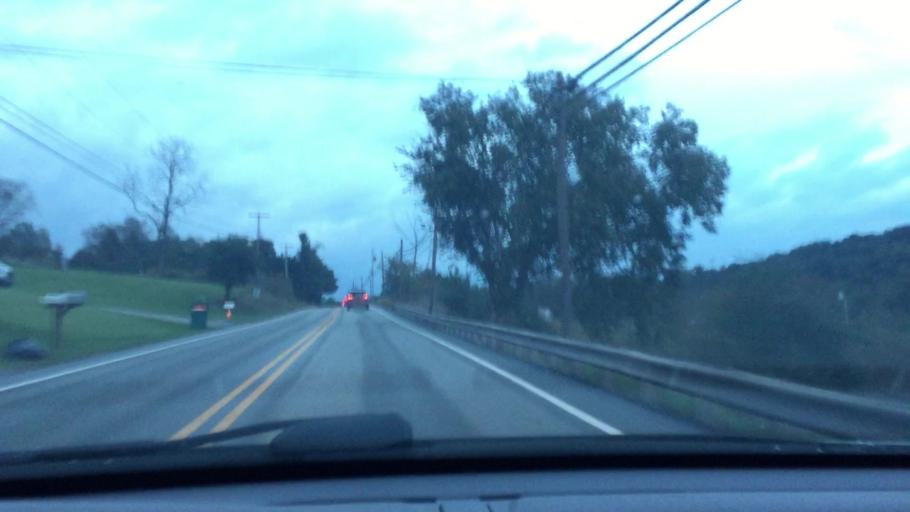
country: US
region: Pennsylvania
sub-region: Washington County
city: McGovern
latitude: 40.1846
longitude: -80.1635
